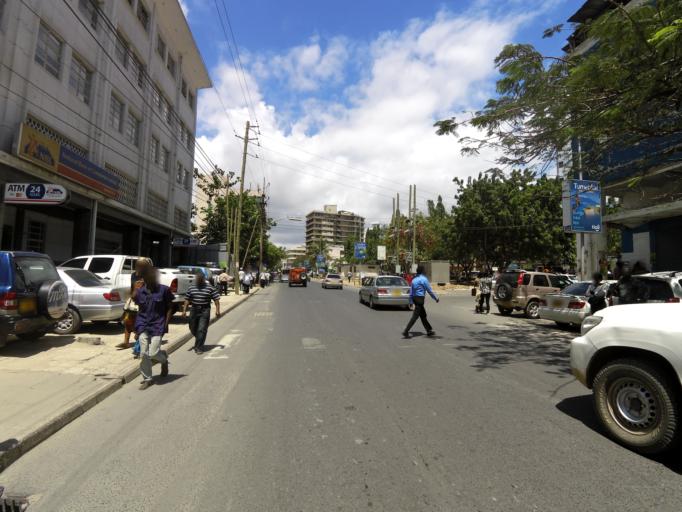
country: TZ
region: Dar es Salaam
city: Dar es Salaam
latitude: -6.8203
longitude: 39.2853
